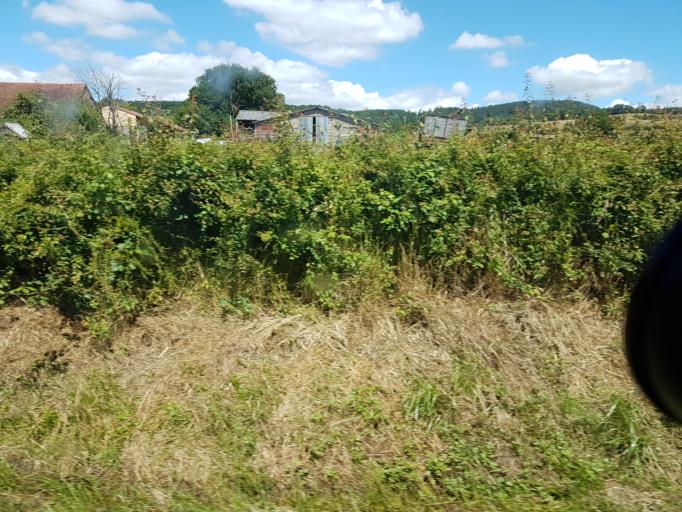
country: FR
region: Bourgogne
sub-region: Departement de Saone-et-Loire
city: Autun
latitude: 47.0523
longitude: 4.2928
